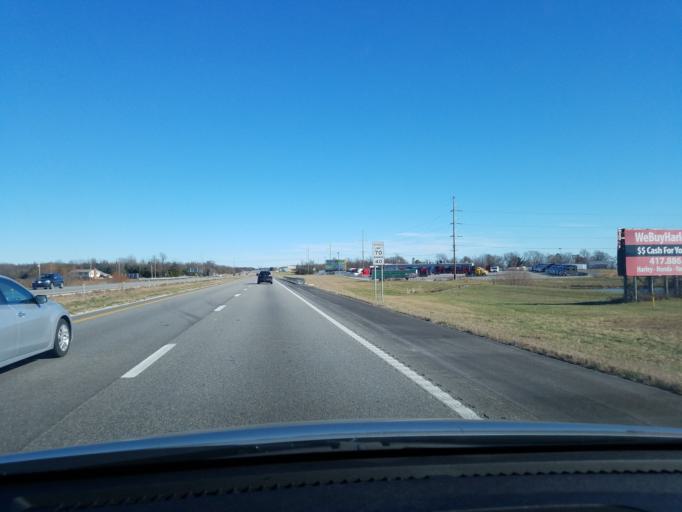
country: US
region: Missouri
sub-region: Greene County
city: Strafford
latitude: 37.2537
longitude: -93.1727
